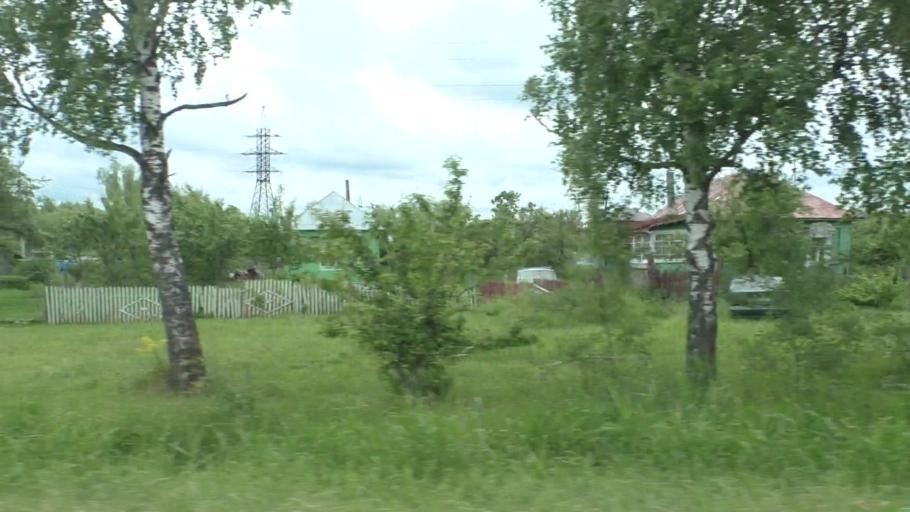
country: RU
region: Moskovskaya
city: Yegor'yevsk
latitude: 55.3979
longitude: 39.0130
